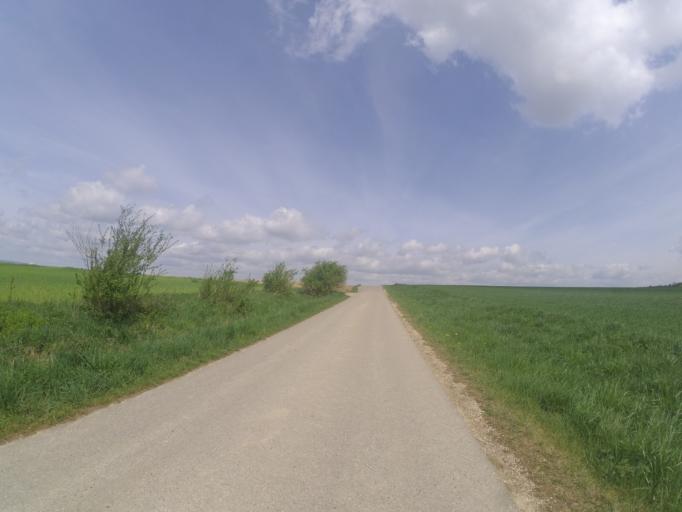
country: DE
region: Baden-Wuerttemberg
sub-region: Tuebingen Region
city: Griesingen
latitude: 48.2516
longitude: 9.7770
